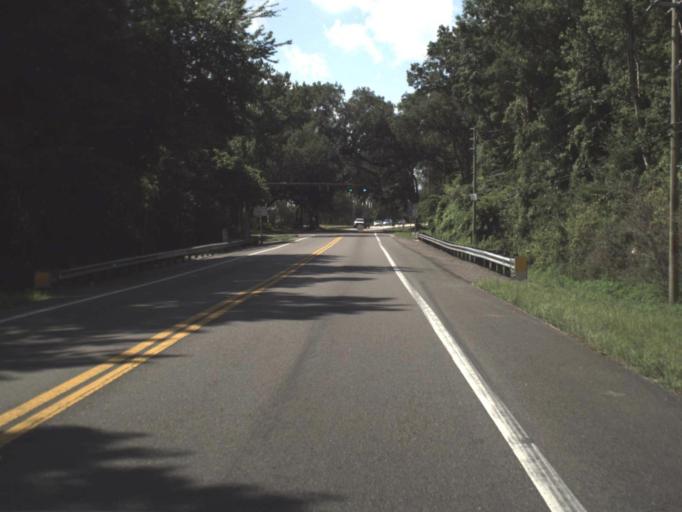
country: US
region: Florida
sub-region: Clay County
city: Green Cove Springs
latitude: 29.9706
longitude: -81.5386
